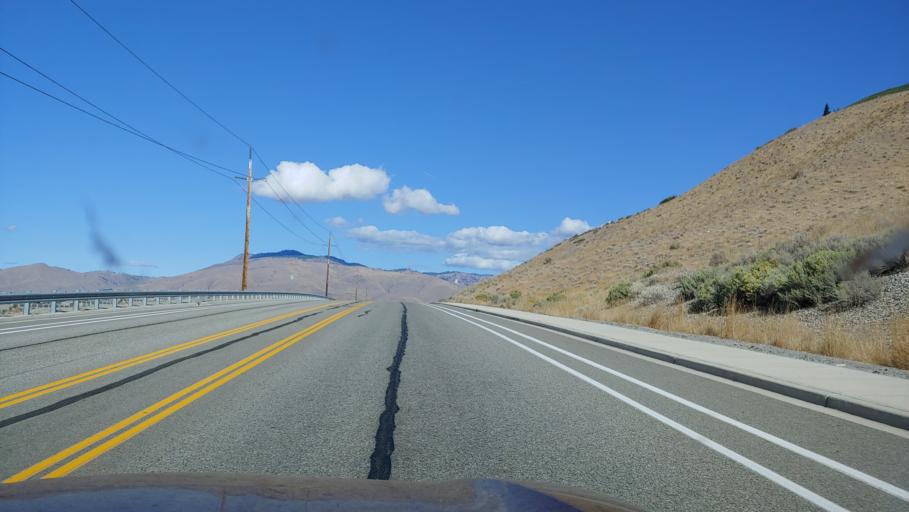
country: US
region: Washington
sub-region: Douglas County
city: East Wenatchee Bench
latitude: 47.4425
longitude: -120.2836
